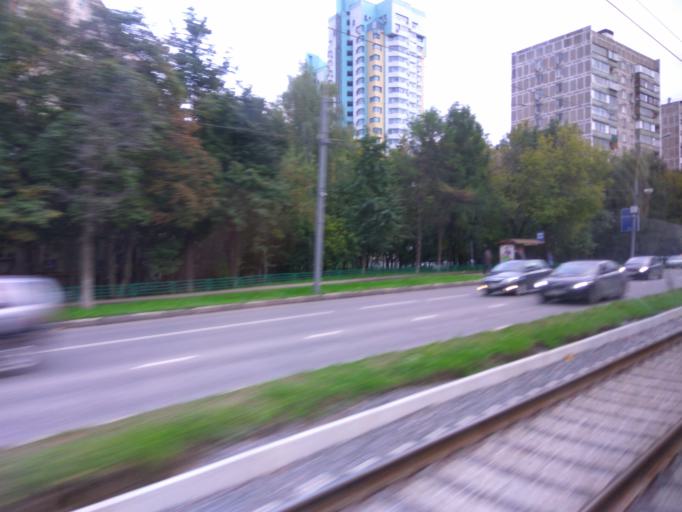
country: RU
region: Moscow
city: Chertanovo Yuzhnoye
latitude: 55.6099
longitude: 37.5911
